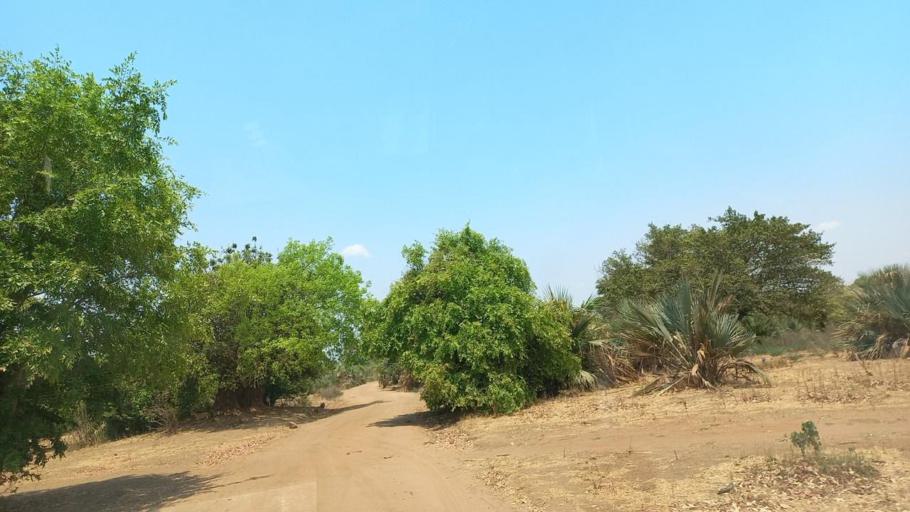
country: ZM
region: Lusaka
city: Luangwa
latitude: -15.1930
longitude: 30.1909
